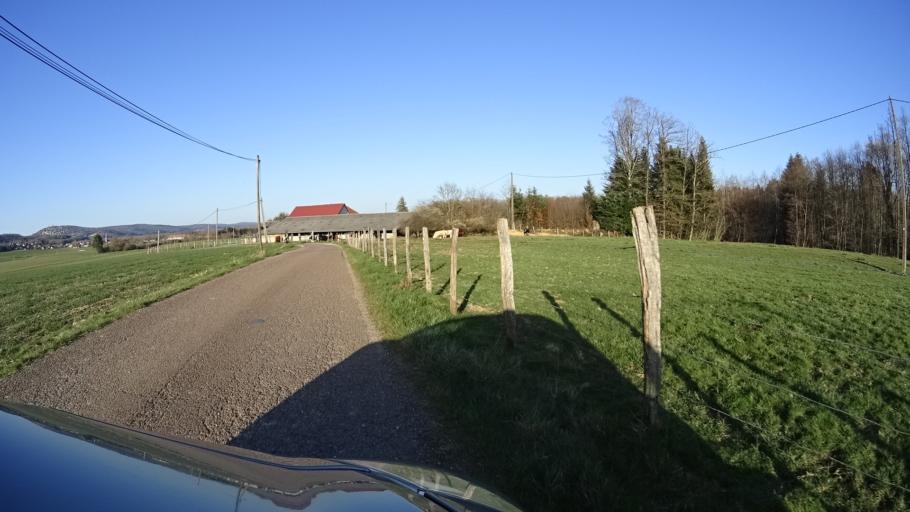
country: FR
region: Franche-Comte
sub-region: Departement du Doubs
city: Morre
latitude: 47.1969
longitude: 6.0596
